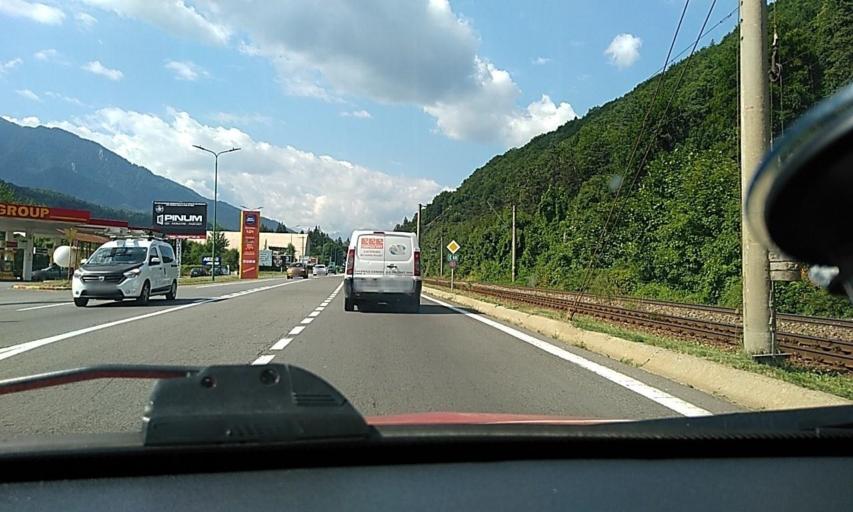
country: RO
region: Brasov
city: Brasov
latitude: 45.6072
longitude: 25.6495
